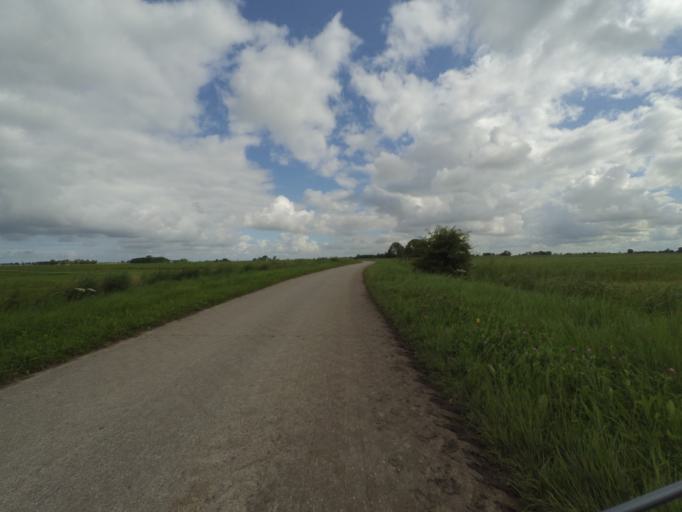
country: NL
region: Friesland
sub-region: Gemeente Kollumerland en Nieuwkruisland
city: Kollum
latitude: 53.2773
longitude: 6.2000
